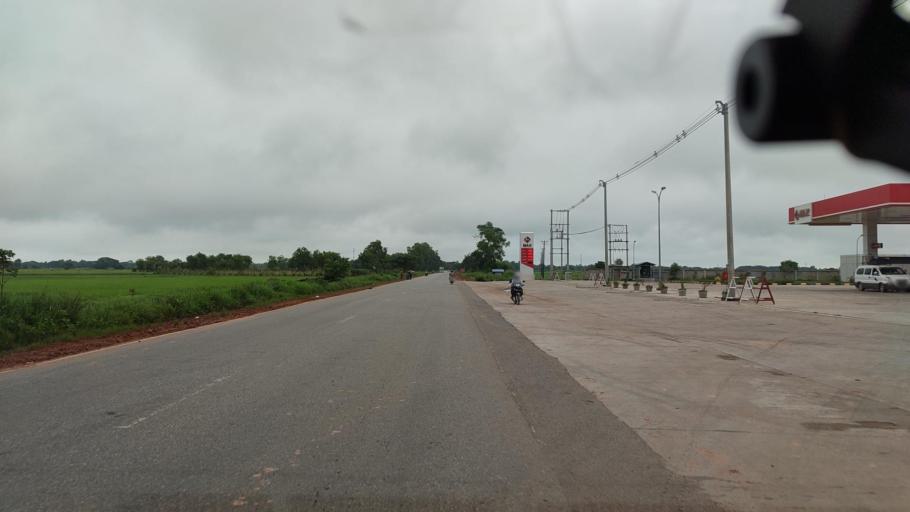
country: MM
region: Bago
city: Tharyarwady
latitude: 17.7047
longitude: 95.7796
